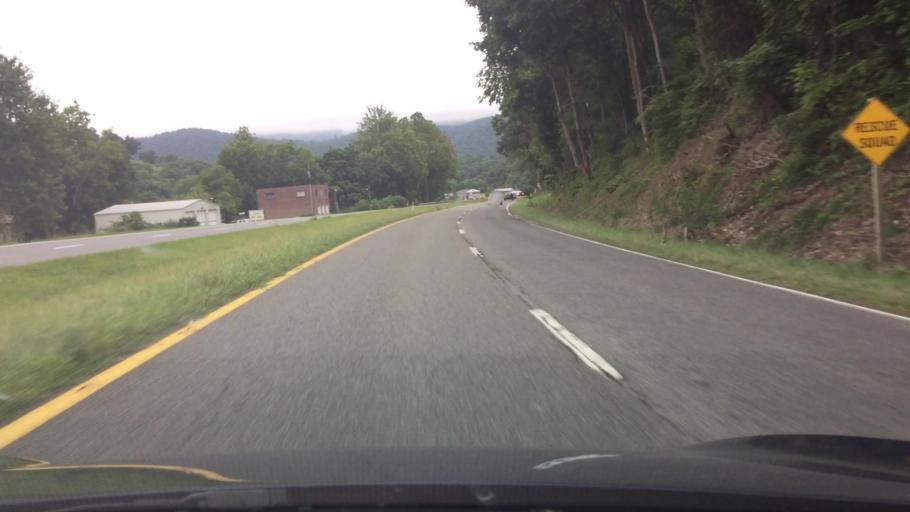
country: US
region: Virginia
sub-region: Montgomery County
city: Shawsville
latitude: 37.1710
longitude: -80.2654
